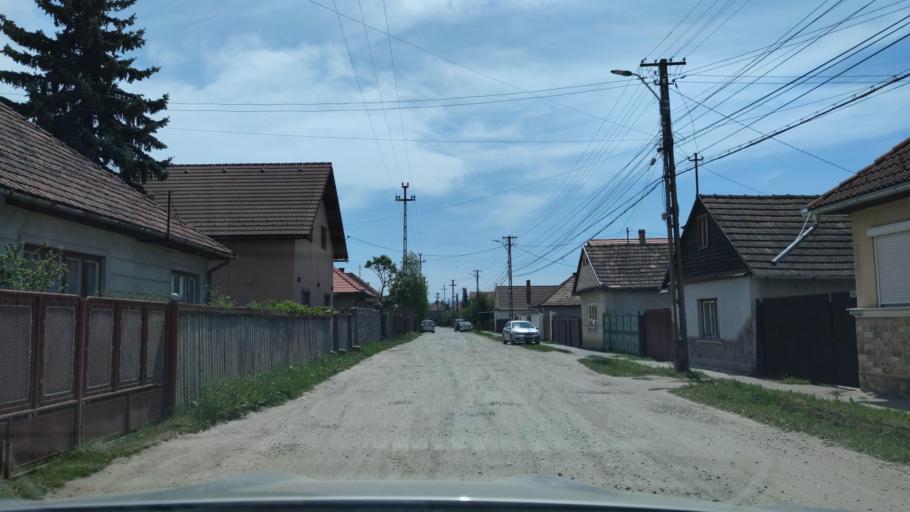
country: RO
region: Harghita
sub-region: Municipiul Gheorgheni
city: Gheorgheni
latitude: 46.7186
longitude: 25.5825
